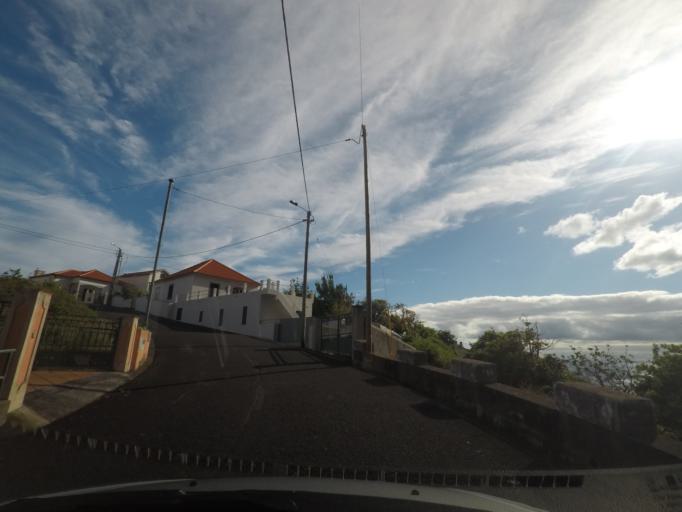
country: PT
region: Madeira
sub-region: Sao Vicente
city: Sao Vicente
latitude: 32.8267
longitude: -16.9883
